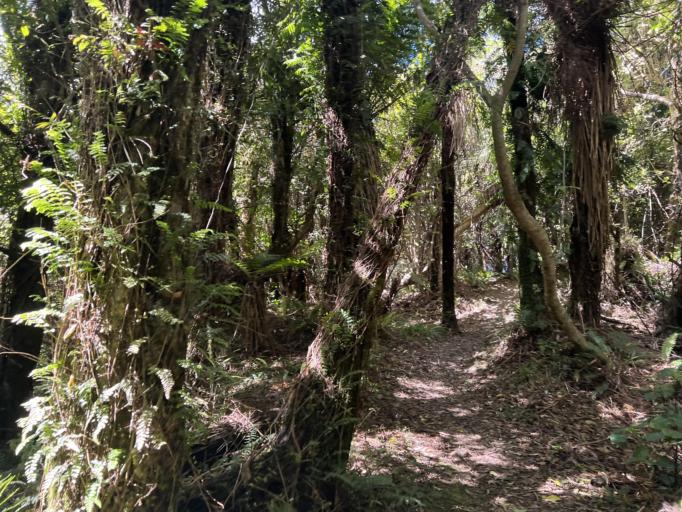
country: NZ
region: Wellington
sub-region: Kapiti Coast District
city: Paraparaumu
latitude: -40.8798
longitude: 175.0906
